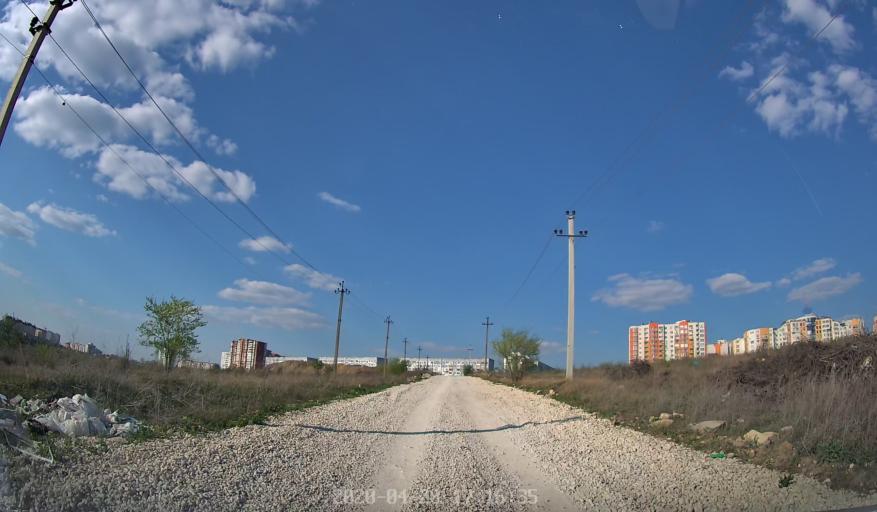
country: MD
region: Chisinau
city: Chisinau
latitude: 46.9718
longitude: 28.8459
